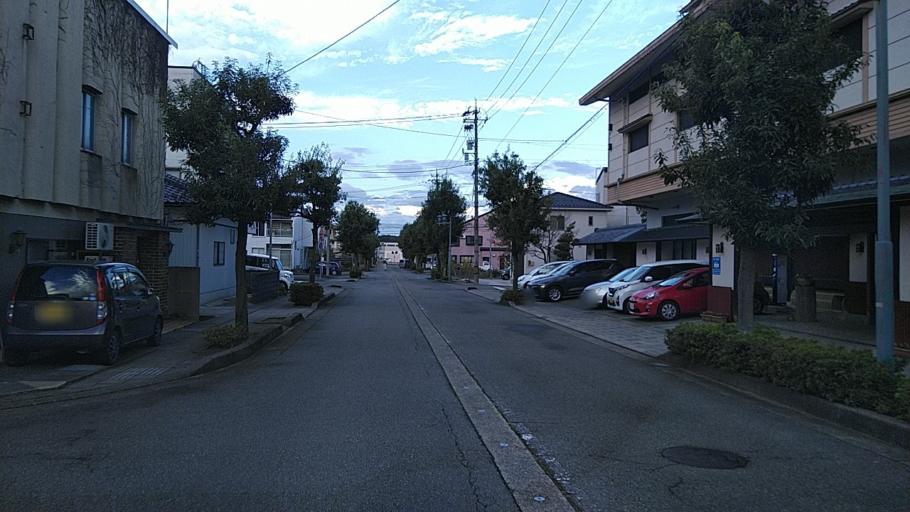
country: JP
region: Ishikawa
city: Komatsu
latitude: 36.2880
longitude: 136.3566
